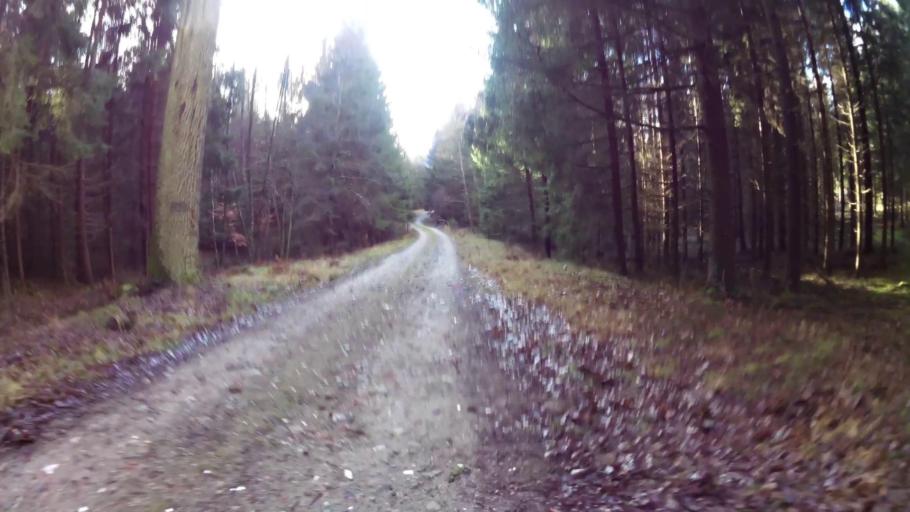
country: PL
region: West Pomeranian Voivodeship
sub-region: Powiat koszalinski
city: Sianow
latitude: 54.1001
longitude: 16.2977
